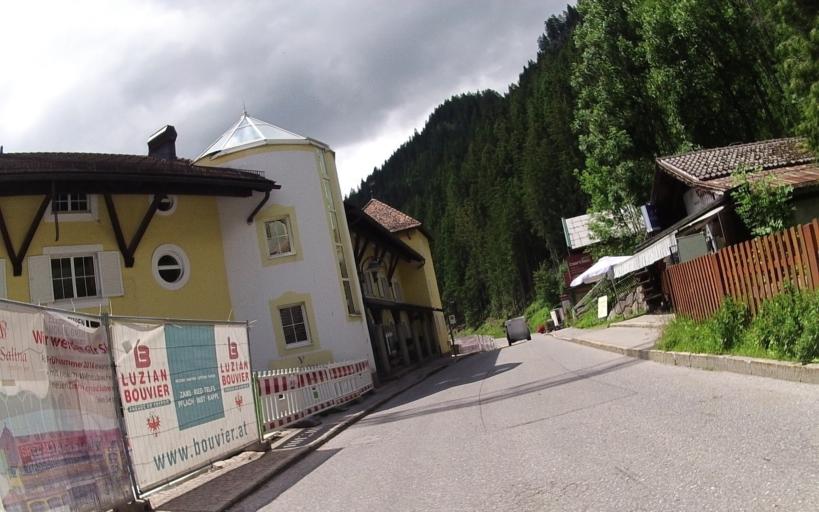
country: AT
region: Tyrol
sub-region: Politischer Bezirk Reutte
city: Graen
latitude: 47.4945
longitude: 10.5837
